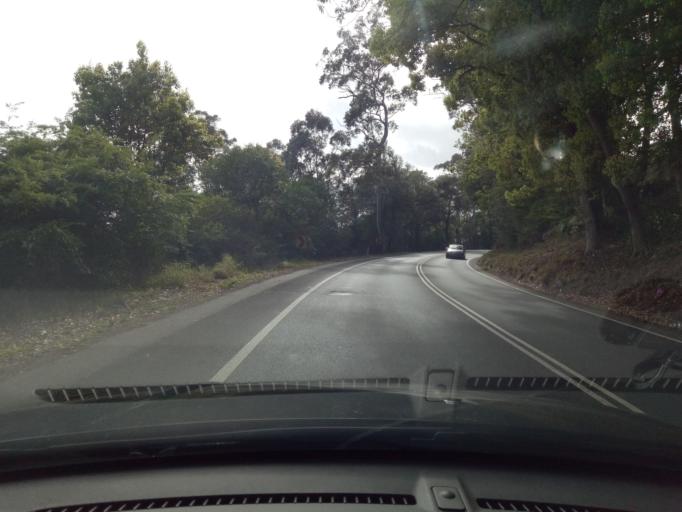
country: AU
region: New South Wales
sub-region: Gosford Shire
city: Lisarow
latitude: -33.3841
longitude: 151.3560
